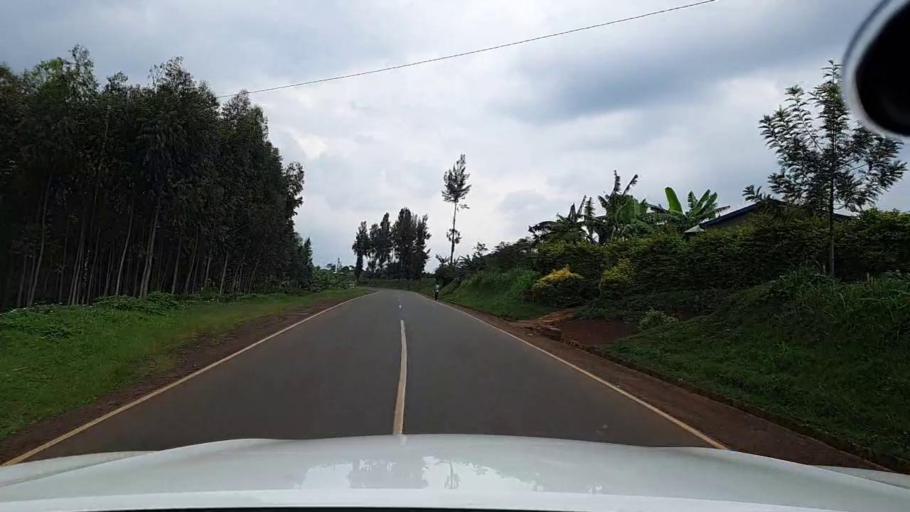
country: RW
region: Western Province
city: Cyangugu
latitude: -2.5932
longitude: 28.9250
